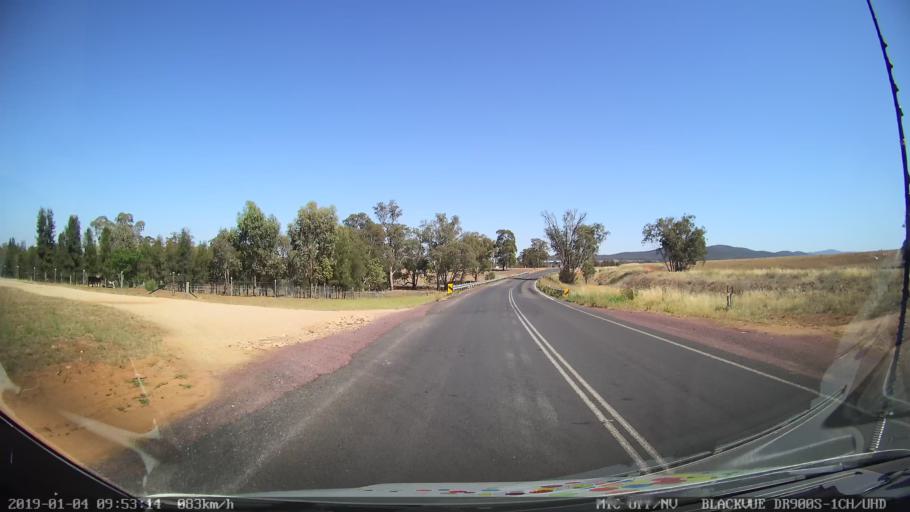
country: AU
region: New South Wales
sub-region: Cabonne
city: Canowindra
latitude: -33.5549
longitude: 148.4213
